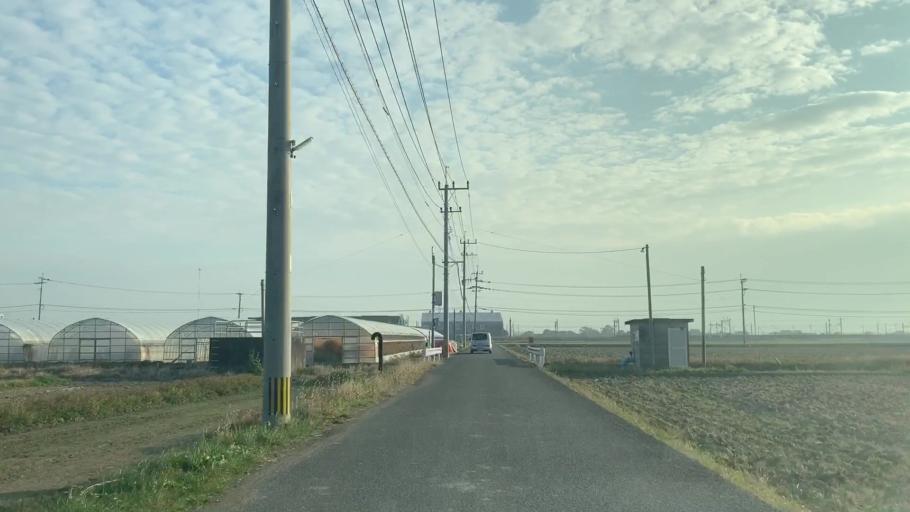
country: JP
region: Saga Prefecture
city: Saga-shi
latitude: 33.2621
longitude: 130.2603
